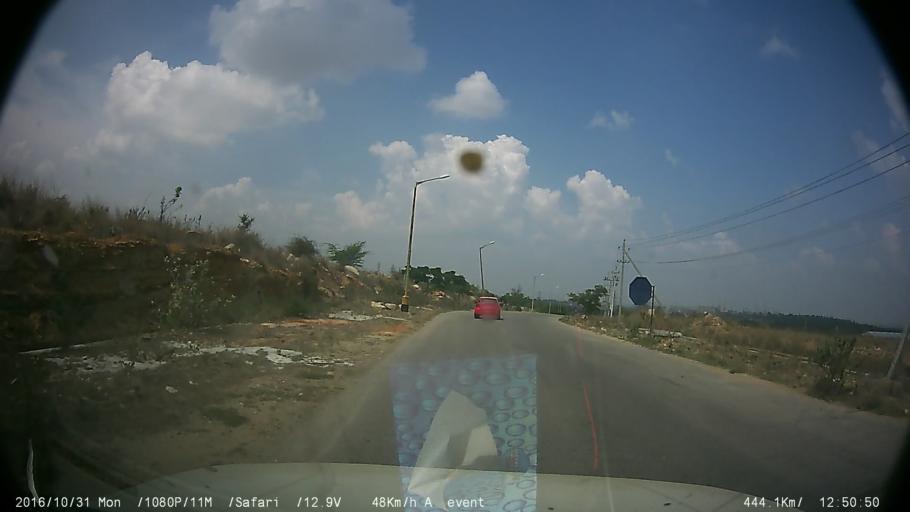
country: IN
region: Karnataka
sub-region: Mysore
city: Mysore
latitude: 12.3595
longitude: 76.5626
